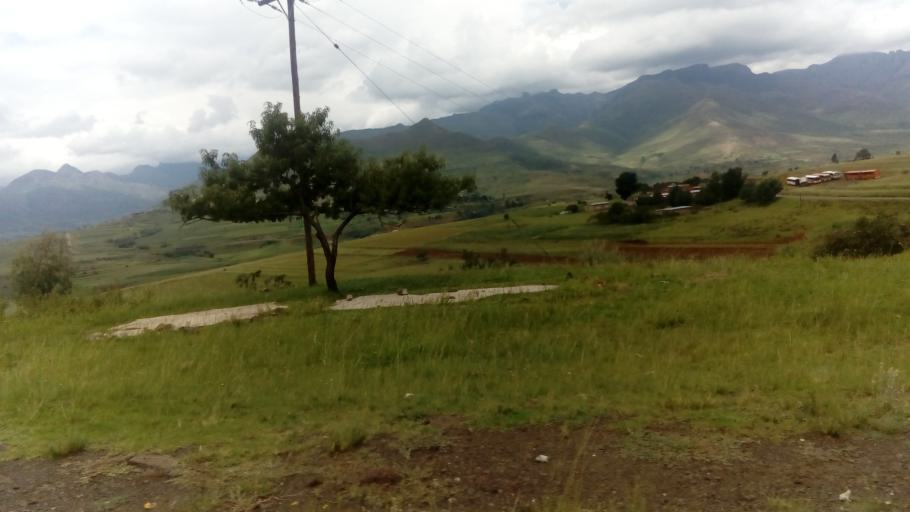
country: LS
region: Leribe
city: Leribe
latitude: -29.0331
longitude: 28.2367
